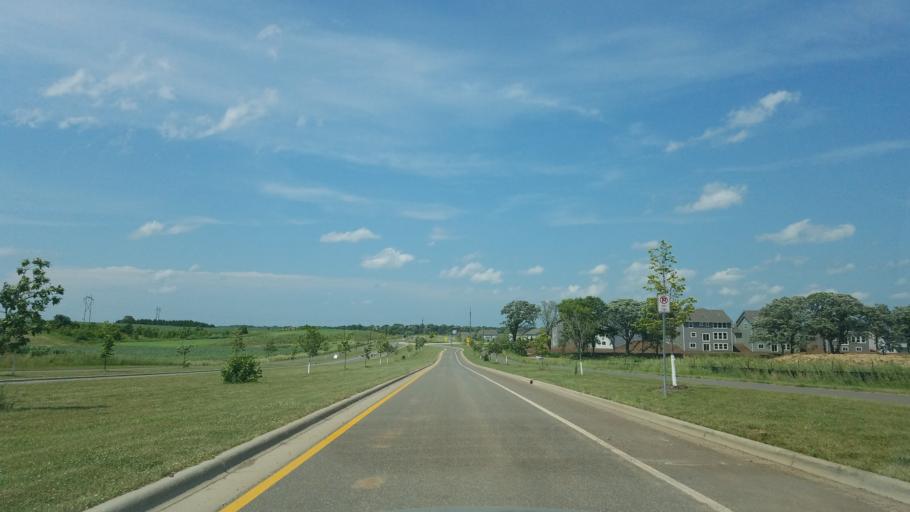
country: US
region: Minnesota
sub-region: Washington County
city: Cottage Grove
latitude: 44.8783
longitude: -92.9236
